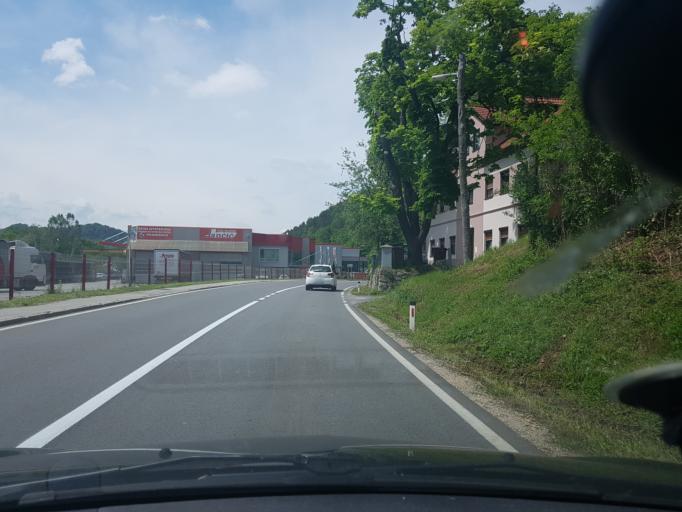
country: SI
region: Store
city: Store
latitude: 46.2228
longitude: 15.3177
